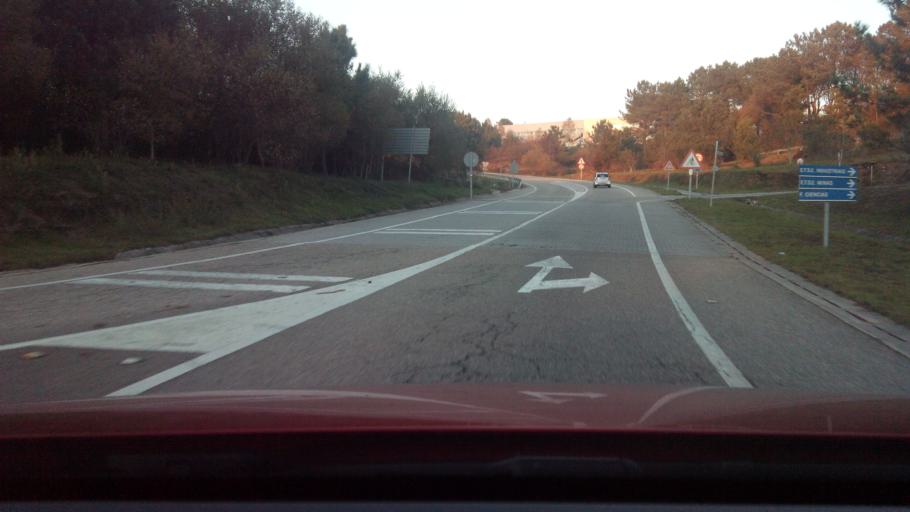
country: ES
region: Galicia
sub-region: Provincia de Pontevedra
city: Vigo
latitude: 42.1677
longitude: -8.6919
